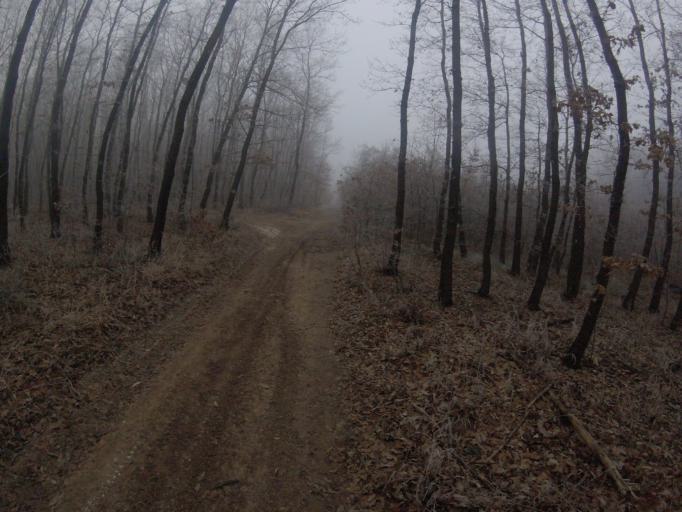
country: HU
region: Fejer
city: Csakvar
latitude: 47.3816
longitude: 18.4145
